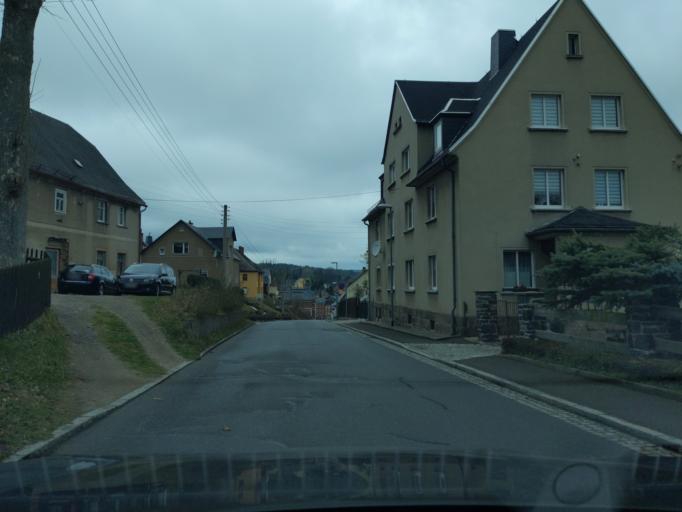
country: DE
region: Saxony
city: Schneeberg
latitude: 50.5810
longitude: 12.6385
